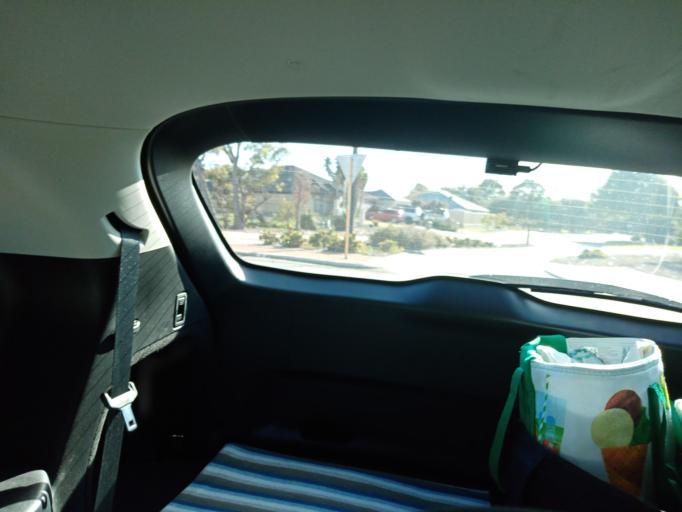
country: AU
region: Western Australia
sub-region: City of Cockburn
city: Beeliar
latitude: -32.1314
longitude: 115.8116
